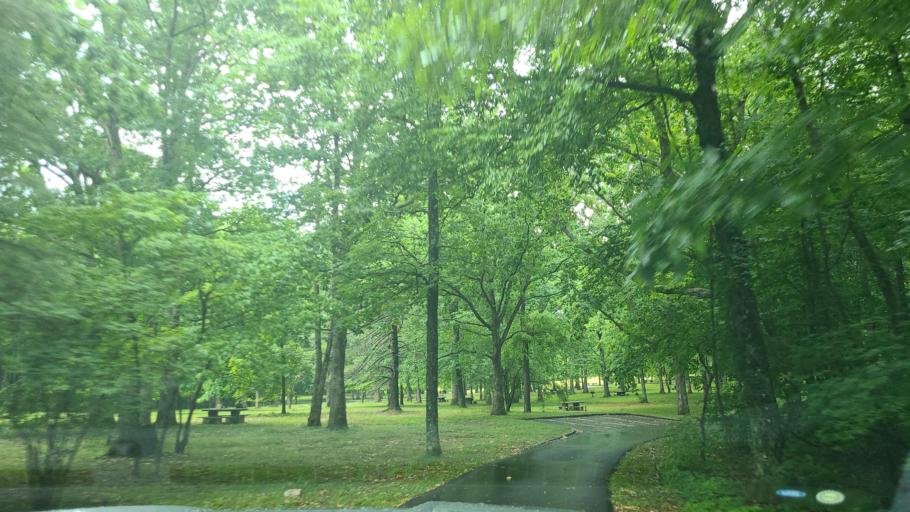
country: US
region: Virginia
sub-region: Floyd County
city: Floyd
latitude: 36.9297
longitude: -80.1852
